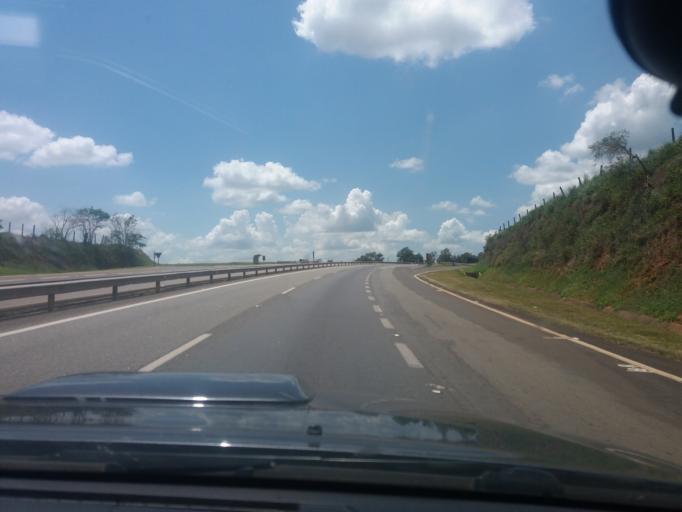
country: BR
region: Sao Paulo
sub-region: Itapetininga
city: Itapetininga
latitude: -23.4905
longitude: -47.9693
